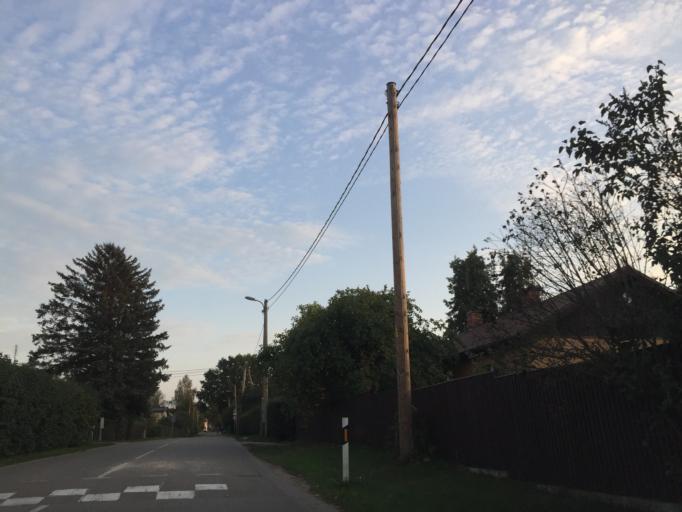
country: LV
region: Baldone
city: Baldone
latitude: 56.7468
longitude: 24.3904
